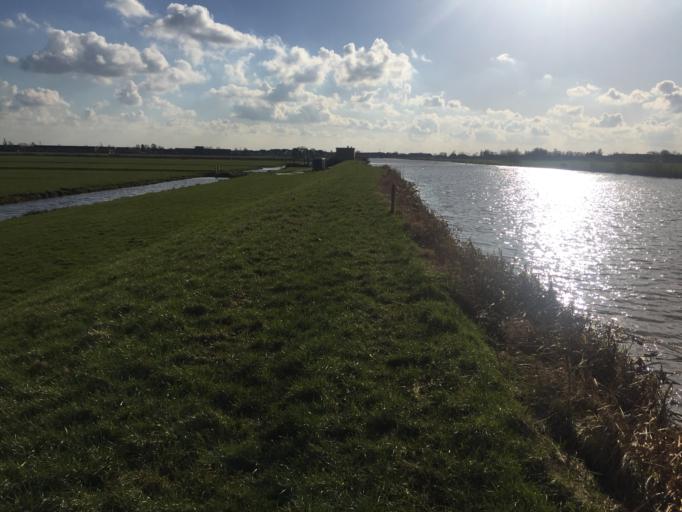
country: NL
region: South Holland
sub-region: Bodegraven-Reeuwijk
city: Bodegraven
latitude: 52.0540
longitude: 4.8015
